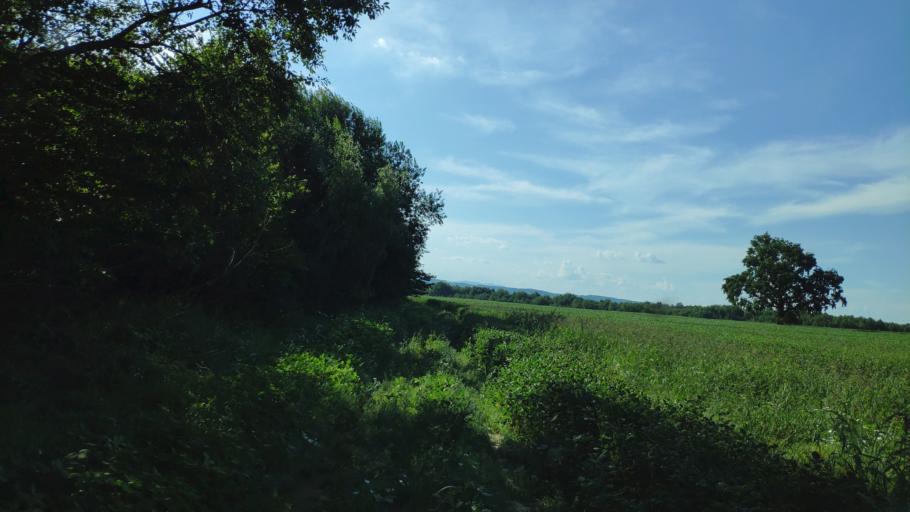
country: SK
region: Presovsky
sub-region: Okres Presov
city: Presov
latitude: 48.9065
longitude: 21.2939
